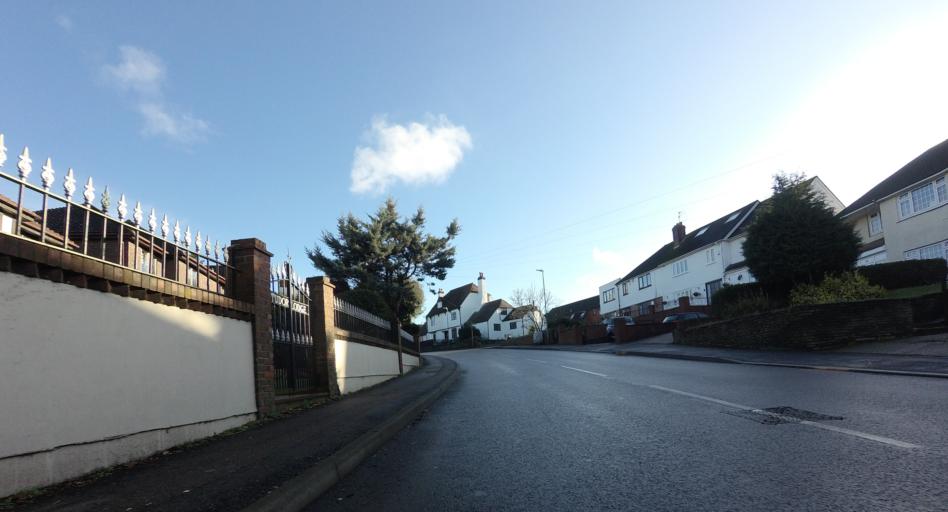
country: GB
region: England
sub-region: Kent
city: Dartford
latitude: 51.4272
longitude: 0.2045
